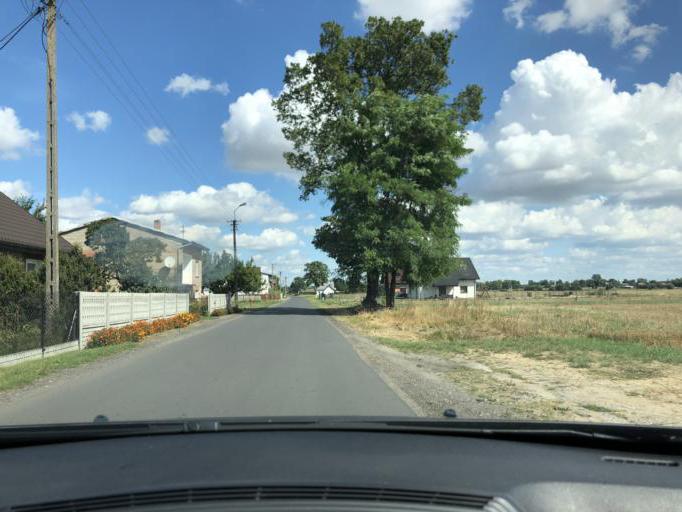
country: PL
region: Lodz Voivodeship
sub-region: Powiat wieruszowski
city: Czastary
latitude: 51.2348
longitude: 18.3563
